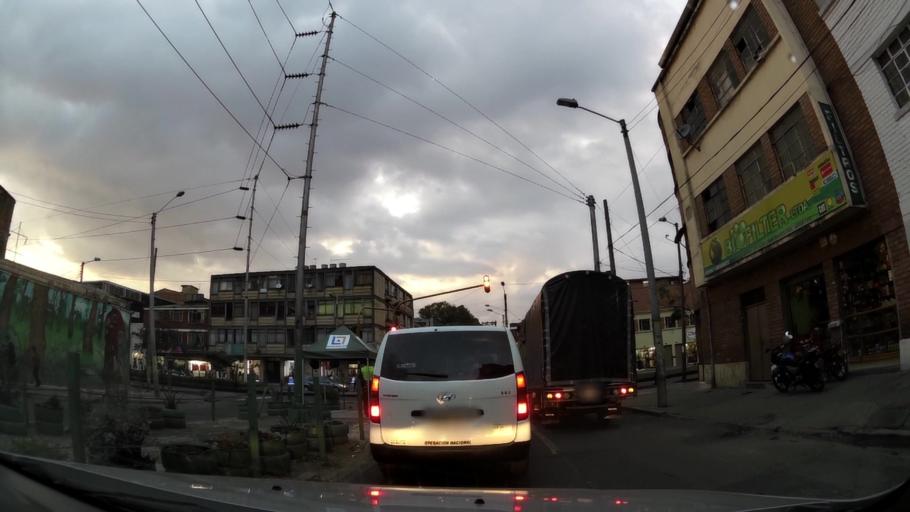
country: CO
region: Bogota D.C.
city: Bogota
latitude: 4.6078
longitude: -74.0896
